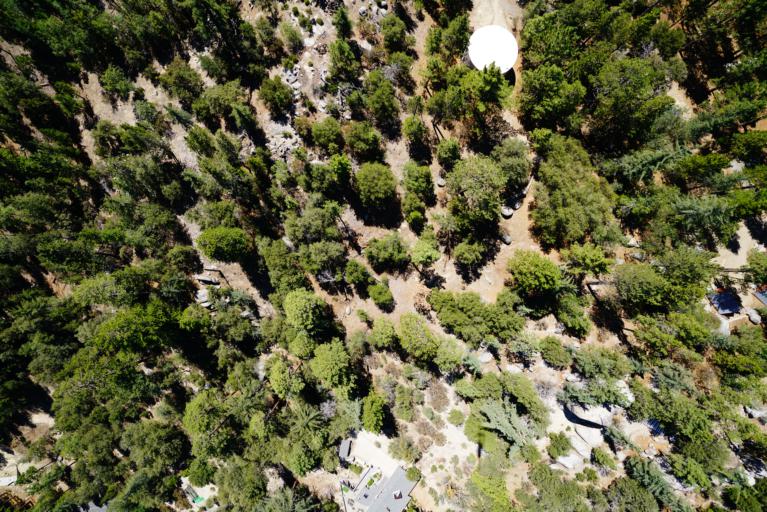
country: US
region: California
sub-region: Riverside County
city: Idyllwild-Pine Cove
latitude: 33.7486
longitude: -116.7290
